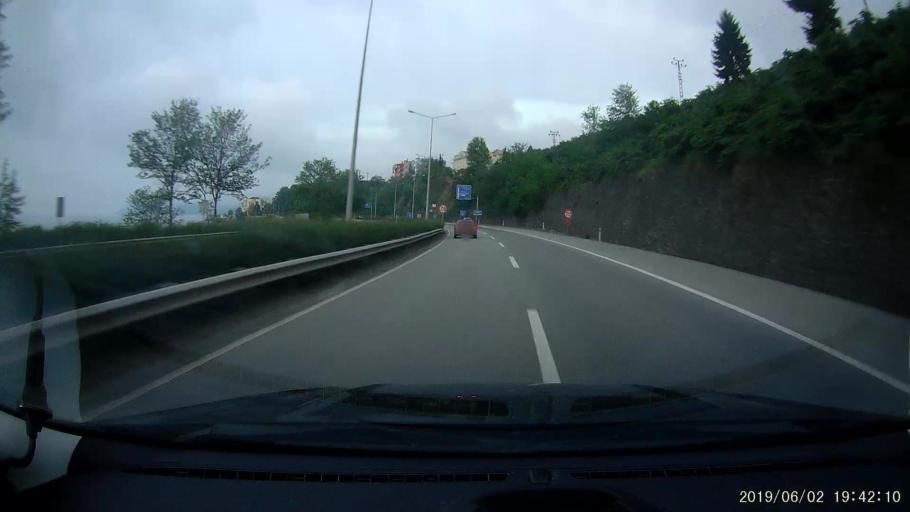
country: TR
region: Giresun
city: Kesap
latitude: 40.9157
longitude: 38.4975
